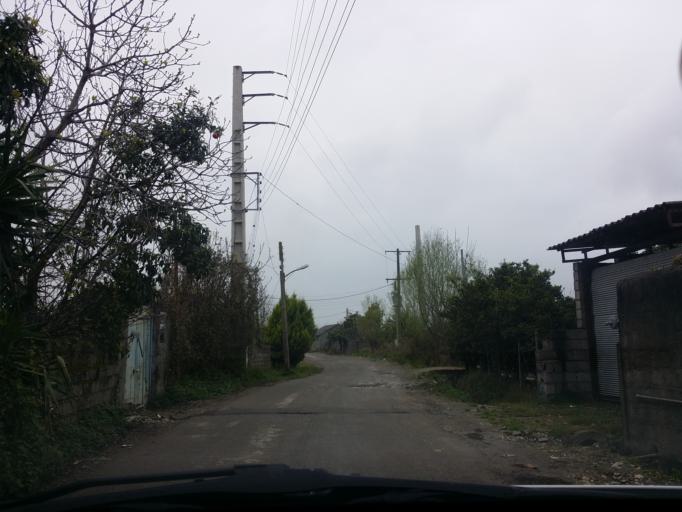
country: IR
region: Mazandaran
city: Chalus
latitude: 36.6687
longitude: 51.3796
